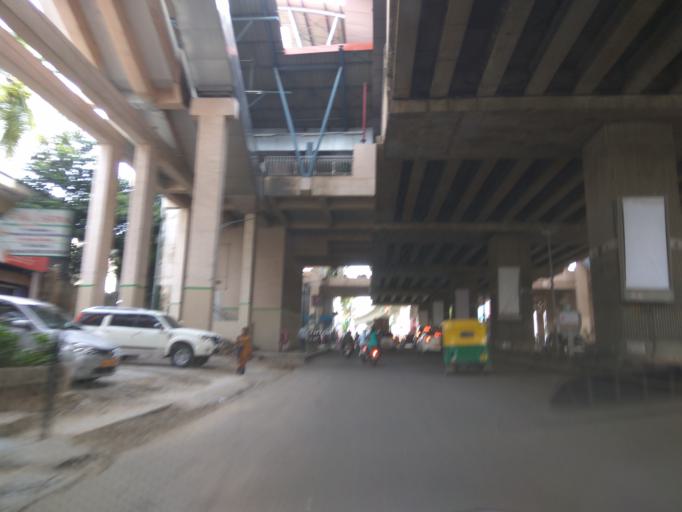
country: IN
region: Karnataka
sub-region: Bangalore Urban
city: Bangalore
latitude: 13.0085
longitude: 77.5489
